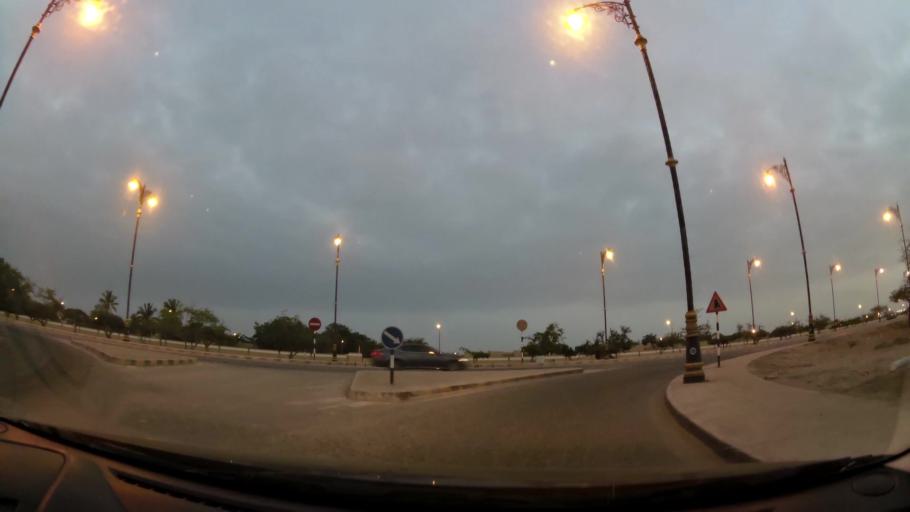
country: OM
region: Zufar
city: Salalah
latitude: 17.0118
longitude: 54.0475
